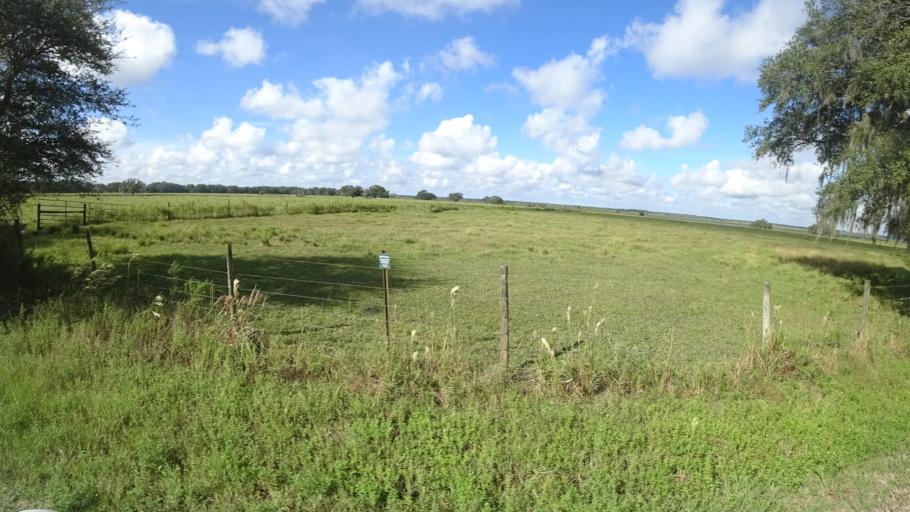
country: US
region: Florida
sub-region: Sarasota County
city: Lake Sarasota
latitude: 27.3204
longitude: -82.2196
